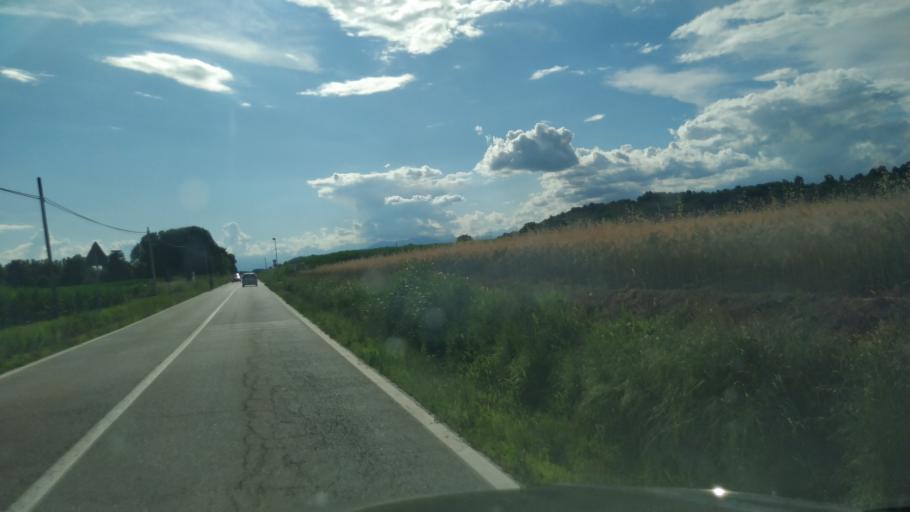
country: IT
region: Piedmont
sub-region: Provincia di Torino
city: Villareggia
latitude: 45.3115
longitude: 7.9967
